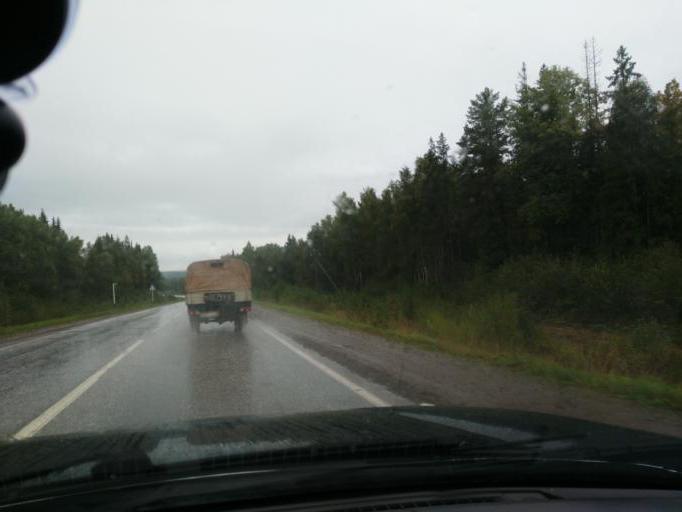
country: RU
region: Perm
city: Osa
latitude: 57.4321
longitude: 55.6236
